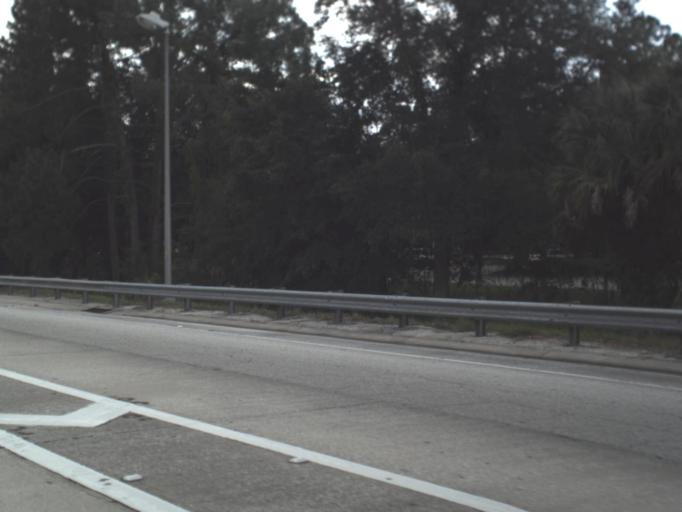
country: US
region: Florida
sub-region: Duval County
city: Jacksonville
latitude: 30.3062
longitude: -81.6170
